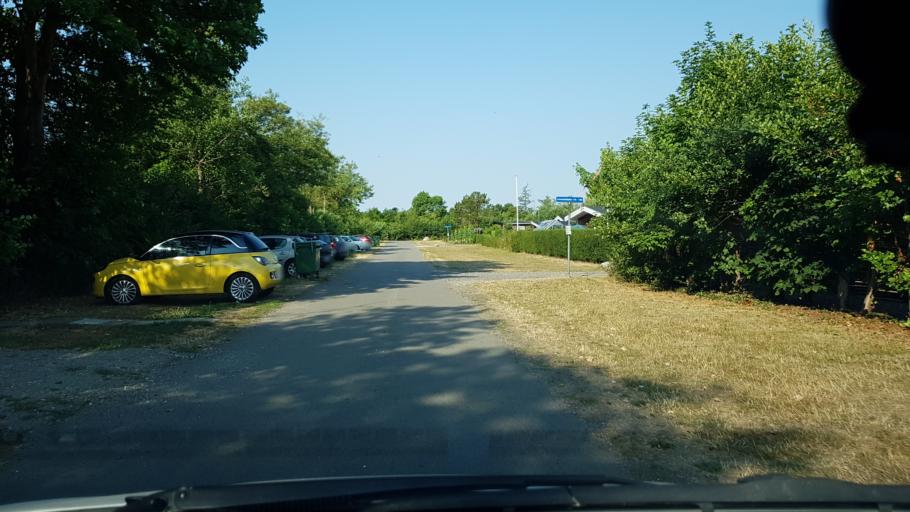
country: DK
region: Capital Region
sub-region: Brondby Kommune
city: Brondbyvester
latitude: 55.6320
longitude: 12.3925
